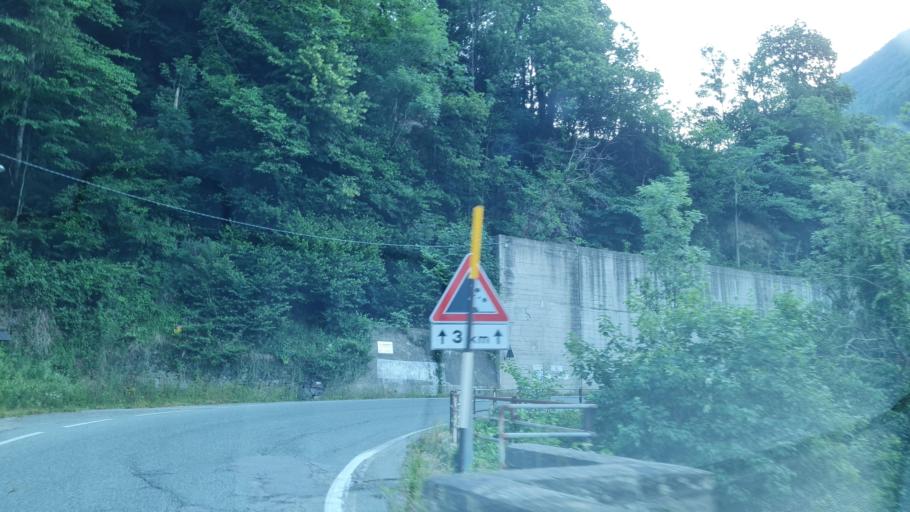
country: IT
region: Piedmont
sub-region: Provincia di Torino
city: Ronco Canavese
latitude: 45.4927
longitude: 7.5395
